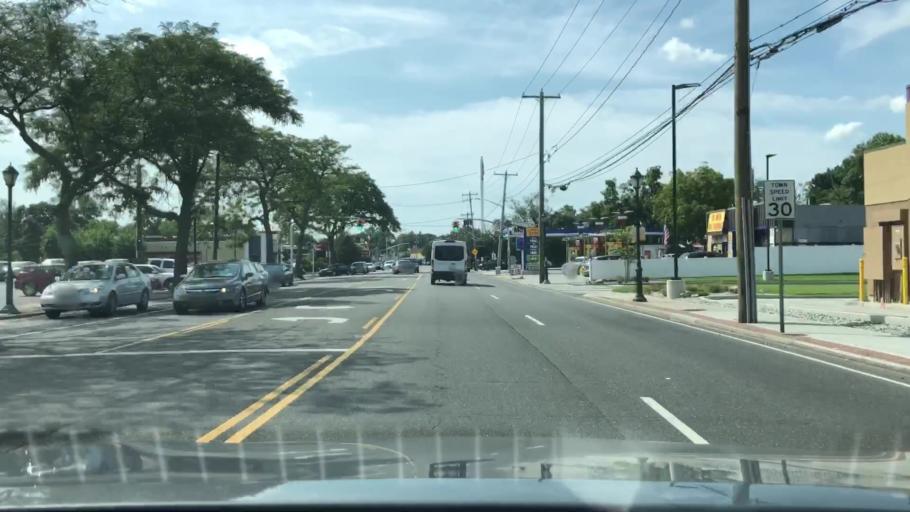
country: US
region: New York
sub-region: Nassau County
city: South Hempstead
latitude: 40.6817
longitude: -73.6152
